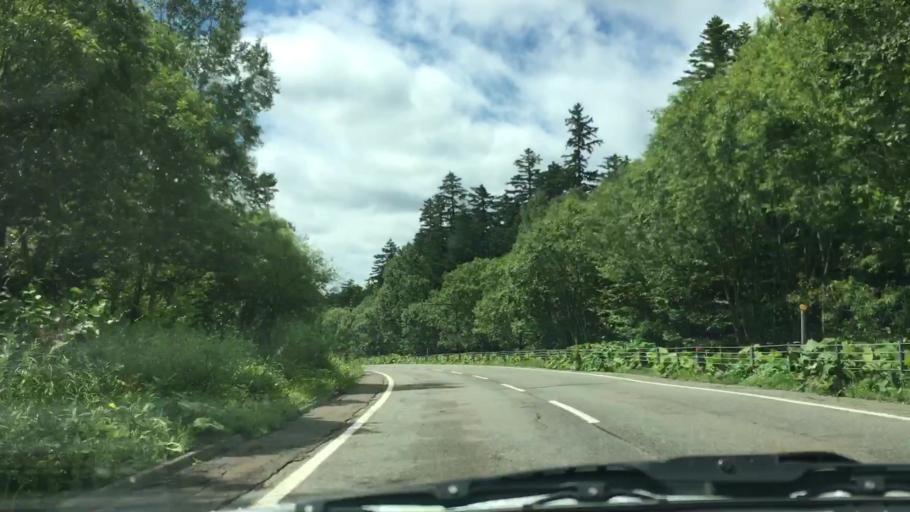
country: JP
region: Hokkaido
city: Kitami
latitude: 43.4267
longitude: 143.9867
